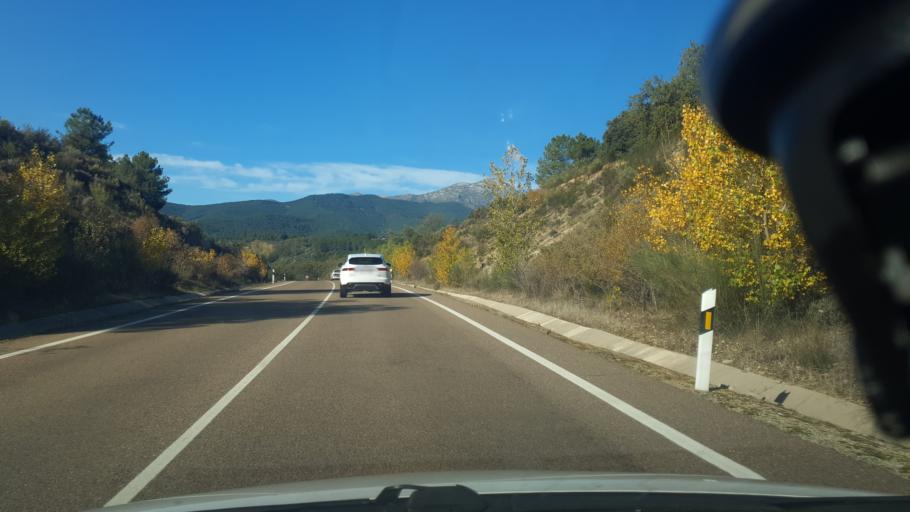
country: ES
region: Castille and Leon
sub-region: Provincia de Avila
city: Arenas de San Pedro
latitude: 40.1896
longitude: -5.0693
